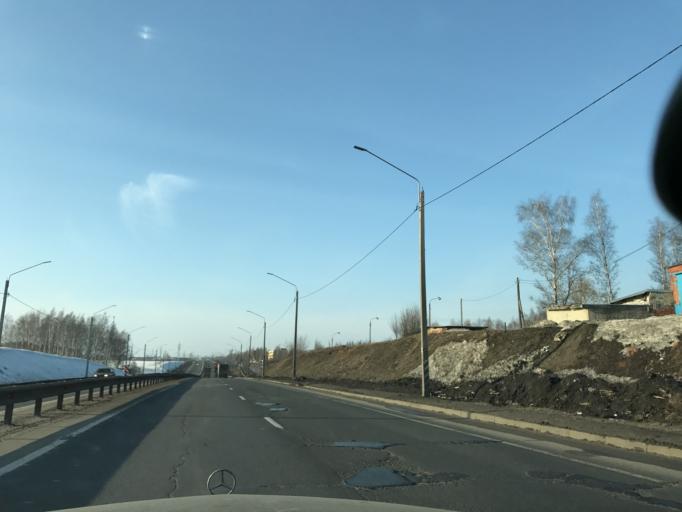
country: RU
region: Vladimir
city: Vyazniki
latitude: 56.2260
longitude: 42.1263
